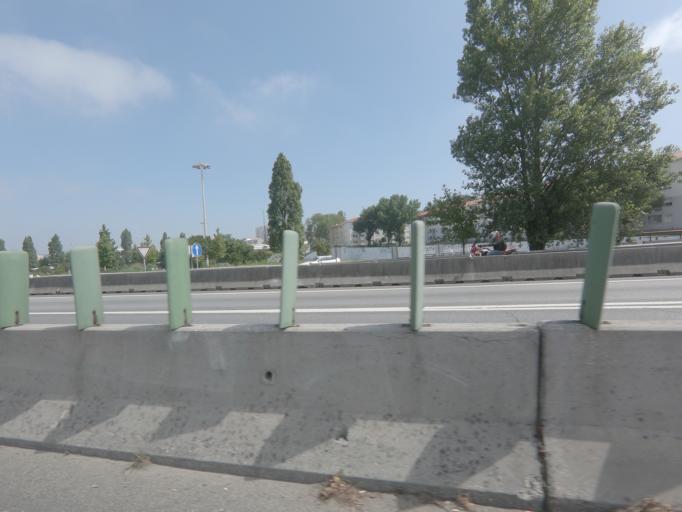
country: PT
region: Porto
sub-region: Matosinhos
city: Senhora da Hora
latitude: 41.1666
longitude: -8.6413
